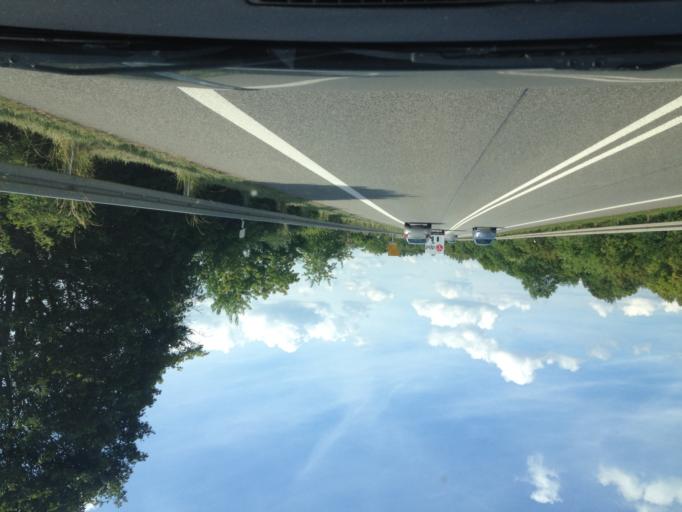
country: DE
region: Saarland
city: Sankt Wendel
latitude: 49.4744
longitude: 7.1465
